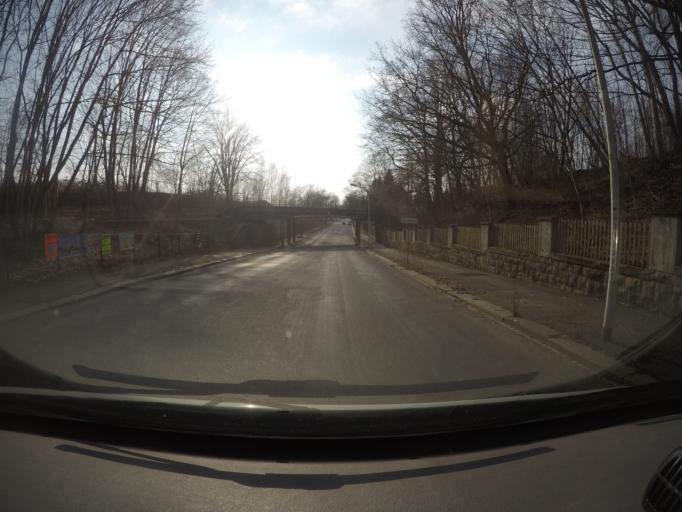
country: DE
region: Saxony
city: Chemnitz
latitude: 50.7970
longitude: 12.9299
